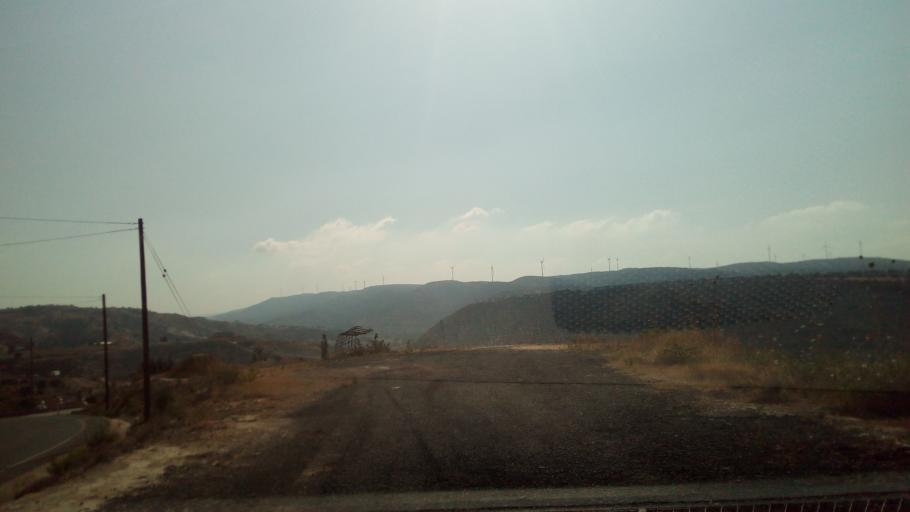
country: CY
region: Limassol
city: Pissouri
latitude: 34.7278
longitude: 32.5721
